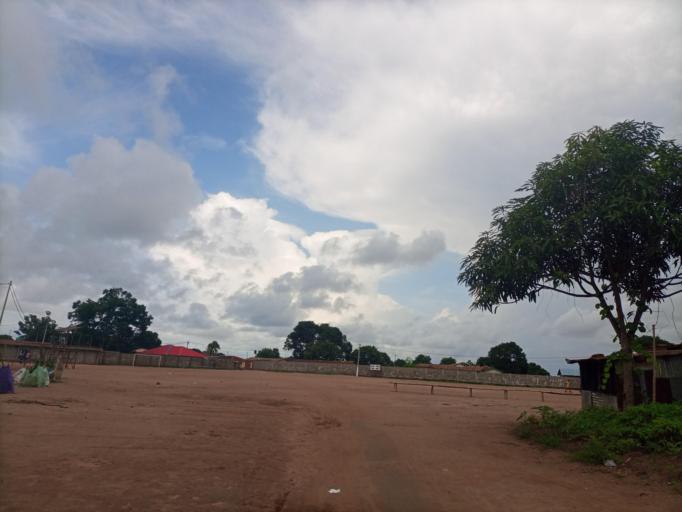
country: SL
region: Northern Province
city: Masoyila
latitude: 8.6081
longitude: -13.1753
